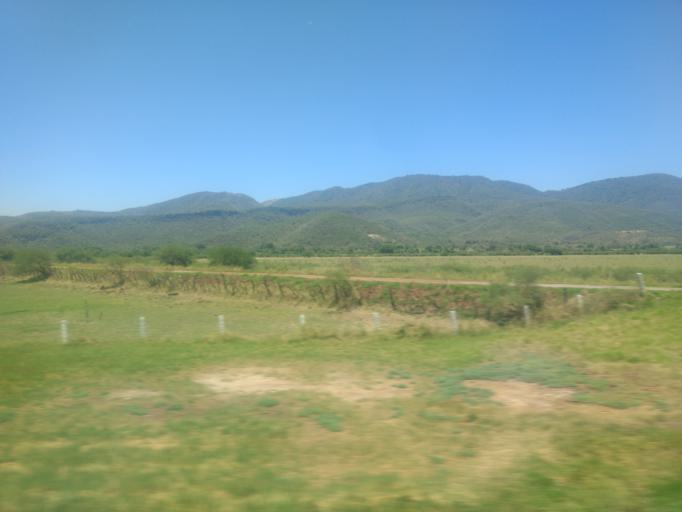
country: MX
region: Jalisco
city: Usmajac
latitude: 19.9419
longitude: -103.5308
